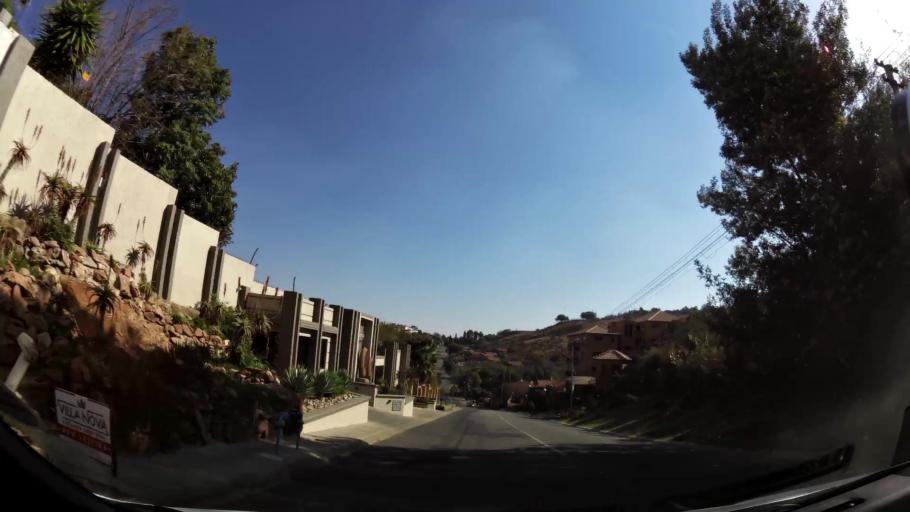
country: ZA
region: Gauteng
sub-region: City of Johannesburg Metropolitan Municipality
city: Johannesburg
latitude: -26.2636
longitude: 28.0481
